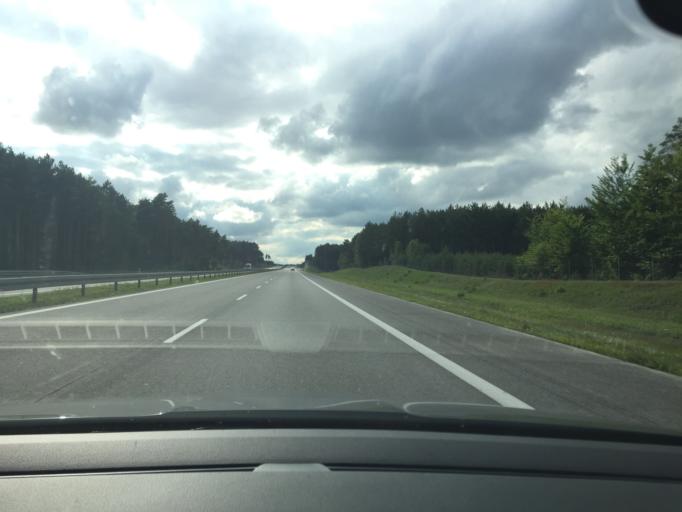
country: PL
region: Lubusz
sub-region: Powiat sulecinski
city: Torzym
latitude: 52.3263
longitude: 15.0522
